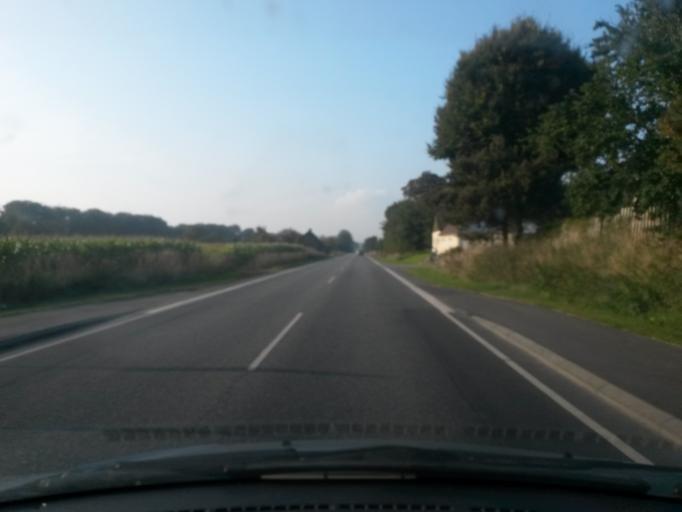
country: DK
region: Central Jutland
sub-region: Syddjurs Kommune
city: Hornslet
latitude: 56.3584
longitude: 10.3383
